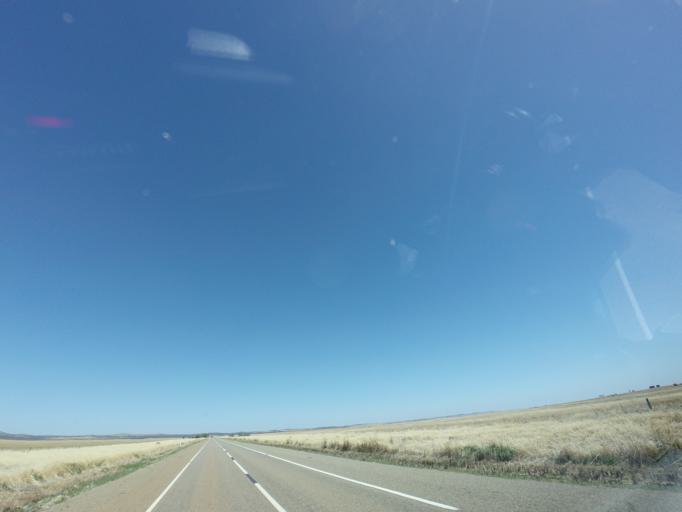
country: AU
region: South Australia
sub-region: Peterborough
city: Peterborough
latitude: -32.8240
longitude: 138.7009
